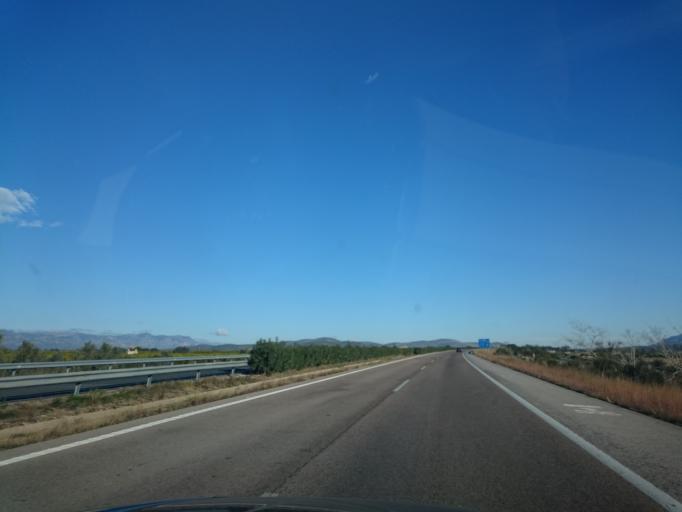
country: ES
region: Catalonia
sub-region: Provincia de Tarragona
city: Ulldecona
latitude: 40.5482
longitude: 0.4208
